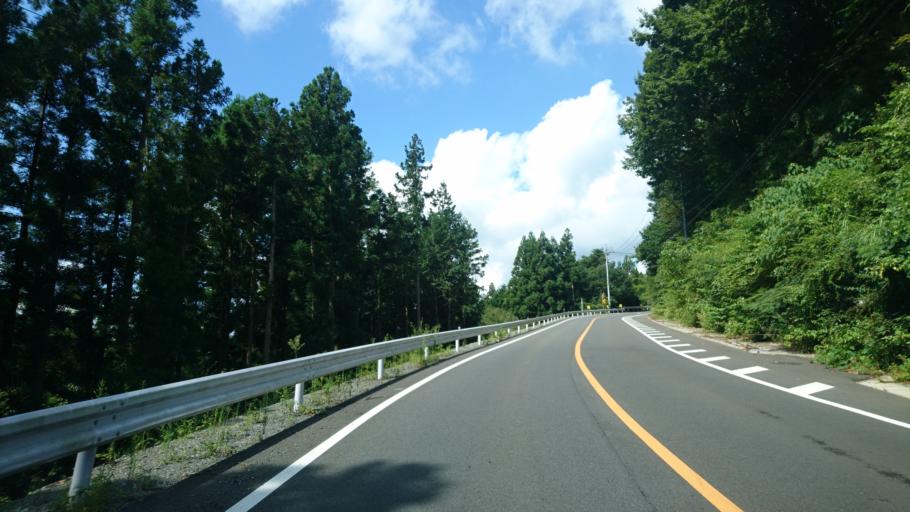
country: JP
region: Gunma
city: Omamacho-omama
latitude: 36.4920
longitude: 139.2745
